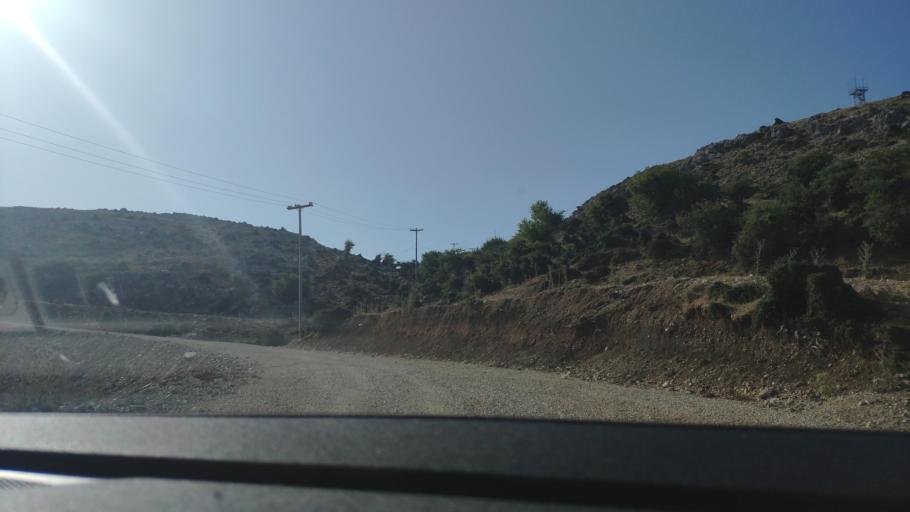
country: GR
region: West Greece
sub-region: Nomos Aitolias kai Akarnanias
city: Monastirakion
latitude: 38.8124
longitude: 20.9800
